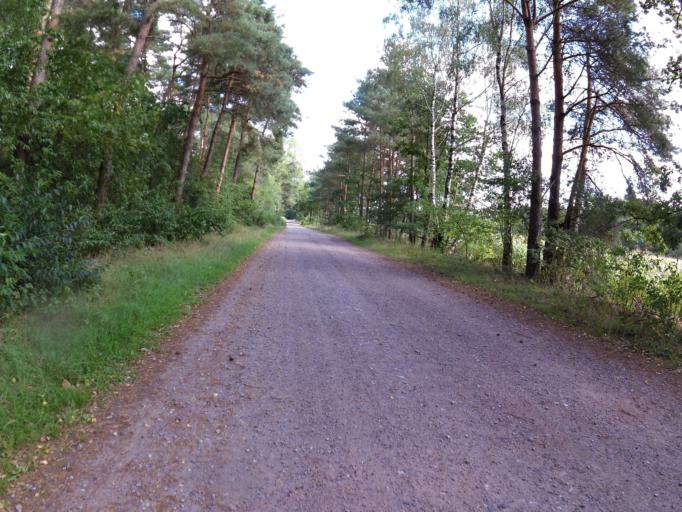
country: DE
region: Lower Saxony
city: Seedorf
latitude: 53.3275
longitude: 9.2444
